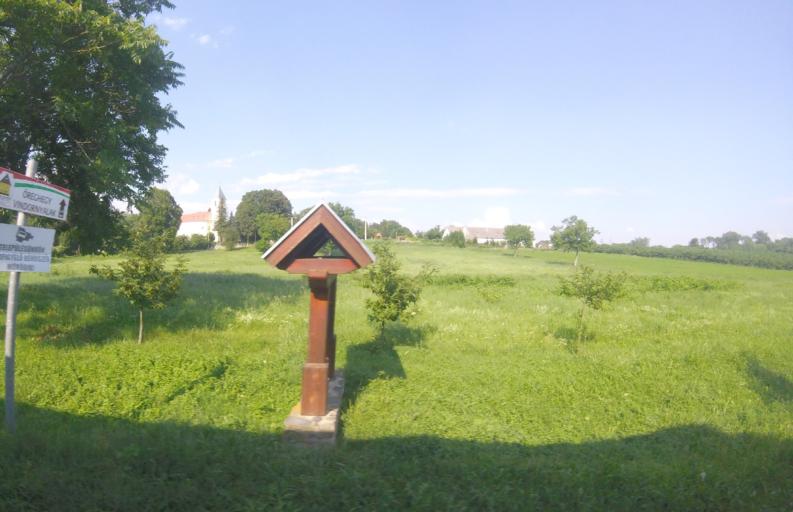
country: HU
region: Zala
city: Cserszegtomaj
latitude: 46.8850
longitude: 17.1948
